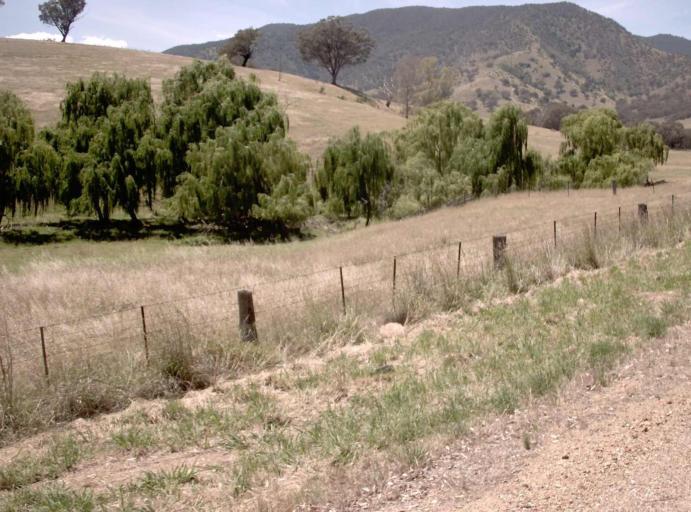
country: AU
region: Victoria
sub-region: East Gippsland
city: Bairnsdale
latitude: -37.1870
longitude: 147.7192
